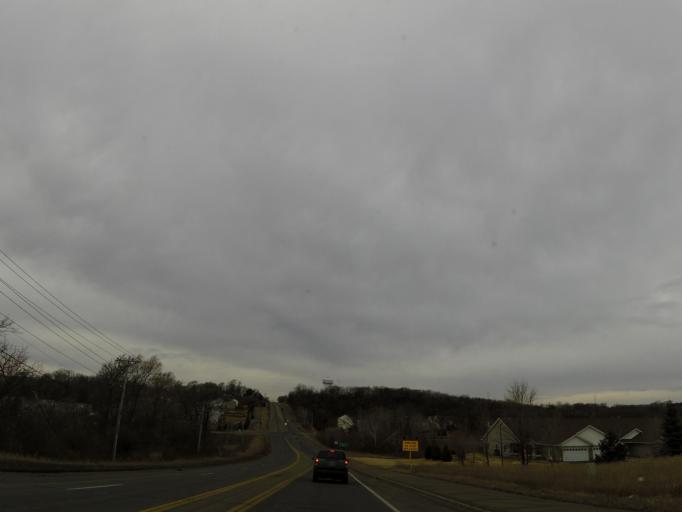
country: US
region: Minnesota
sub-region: Washington County
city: Cottage Grove
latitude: 44.8479
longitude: -92.9557
